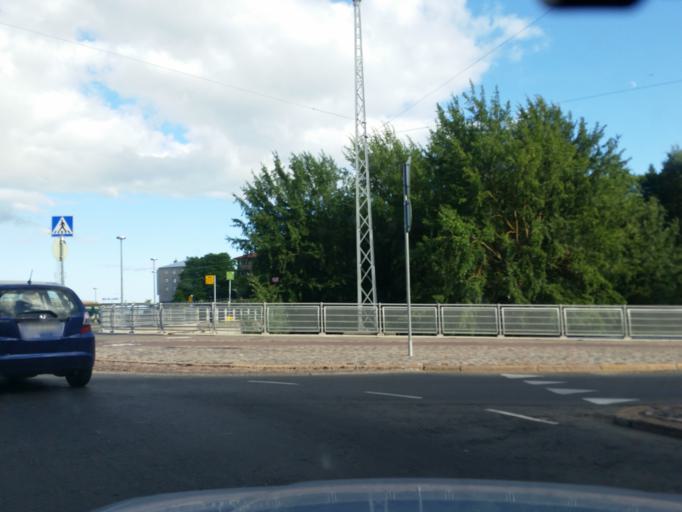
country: FI
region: Uusimaa
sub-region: Helsinki
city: Helsinki
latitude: 60.1611
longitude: 24.9563
